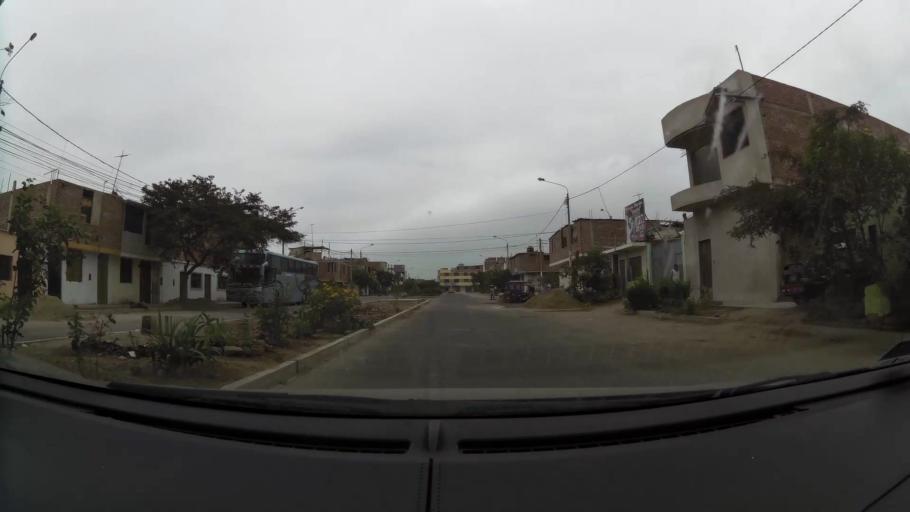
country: PE
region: La Libertad
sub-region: Provincia de Trujillo
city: La Esperanza
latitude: -8.0771
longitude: -79.0563
